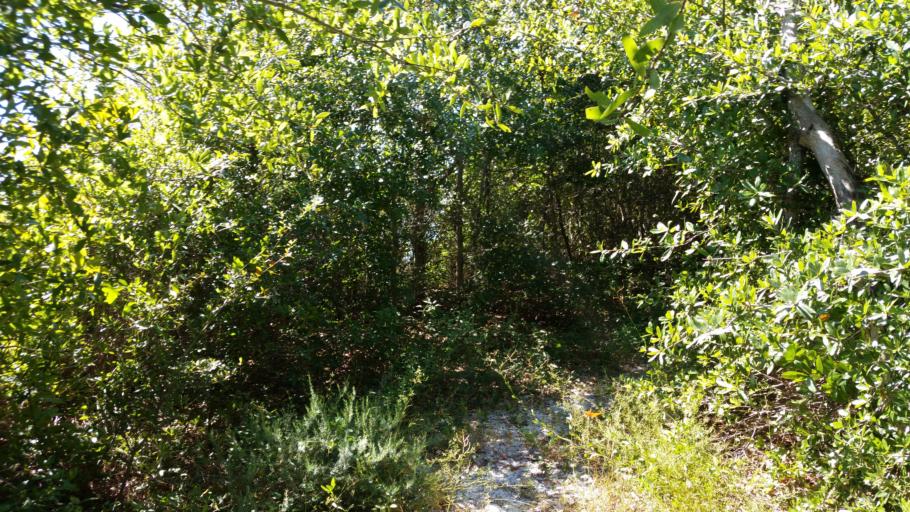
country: US
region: Florida
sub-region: Santa Rosa County
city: Gulf Breeze
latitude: 30.3594
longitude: -87.1496
